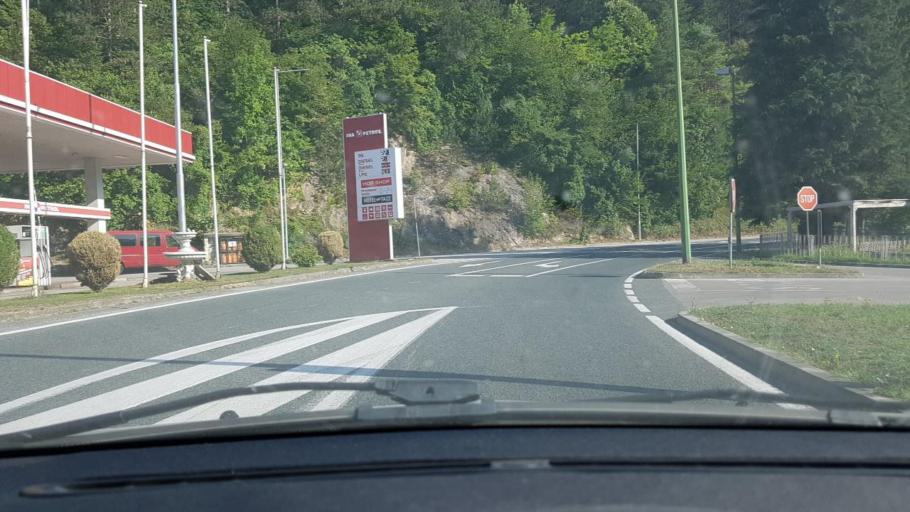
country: BA
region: Federation of Bosnia and Herzegovina
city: Ostrozac
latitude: 44.8977
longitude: 15.9343
